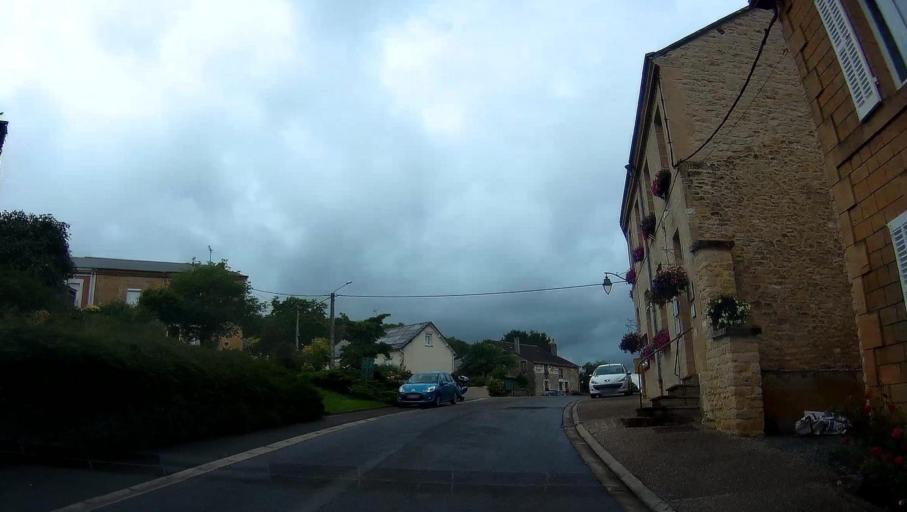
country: FR
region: Champagne-Ardenne
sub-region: Departement des Ardennes
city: Rimogne
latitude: 49.7712
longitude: 4.4710
